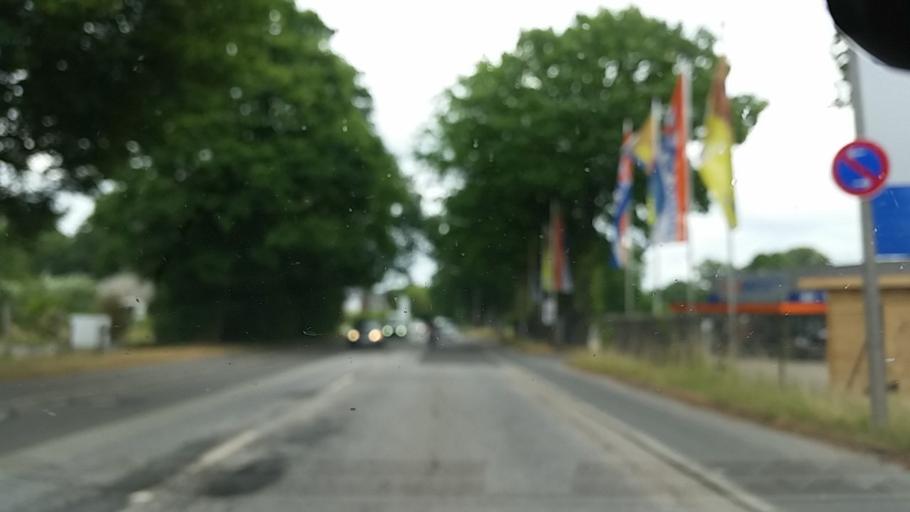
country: DE
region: Hamburg
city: Lemsahl-Mellingstedt
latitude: 53.6983
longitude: 10.0518
